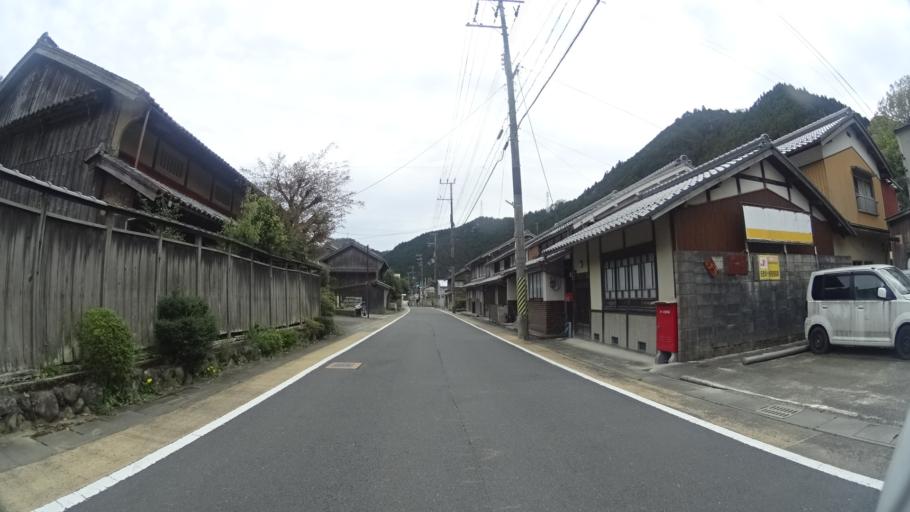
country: JP
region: Kyoto
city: Kameoka
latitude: 35.1554
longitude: 135.5041
